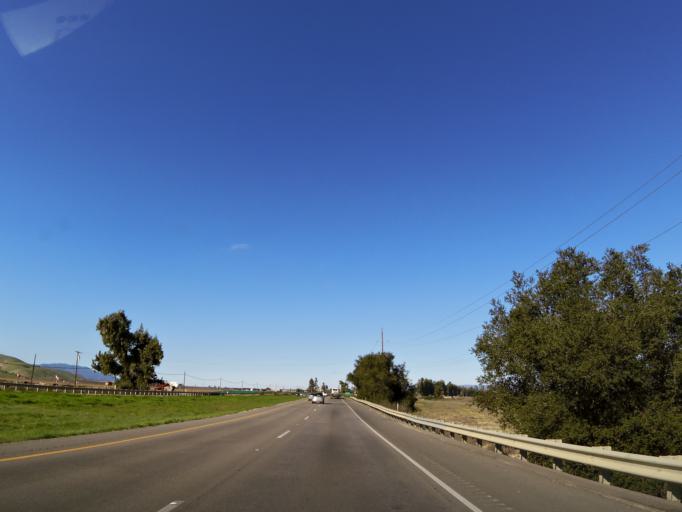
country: US
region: California
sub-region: Monterey County
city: King City
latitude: 36.2253
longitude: -121.1710
